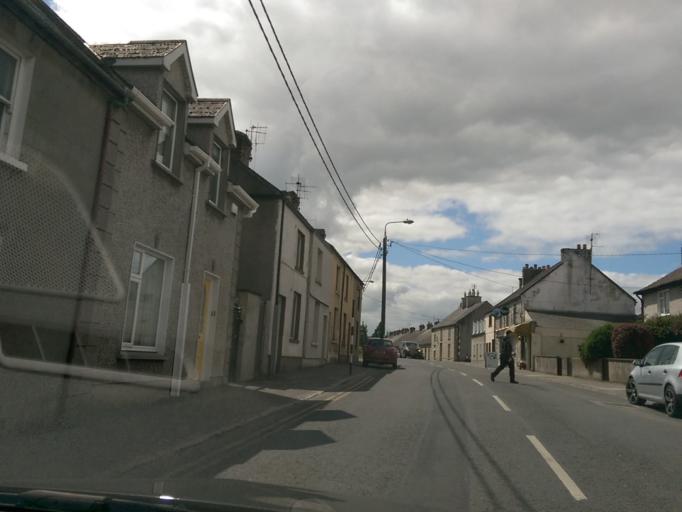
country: IE
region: Munster
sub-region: North Tipperary
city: Nenagh
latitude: 52.8612
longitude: -8.2028
